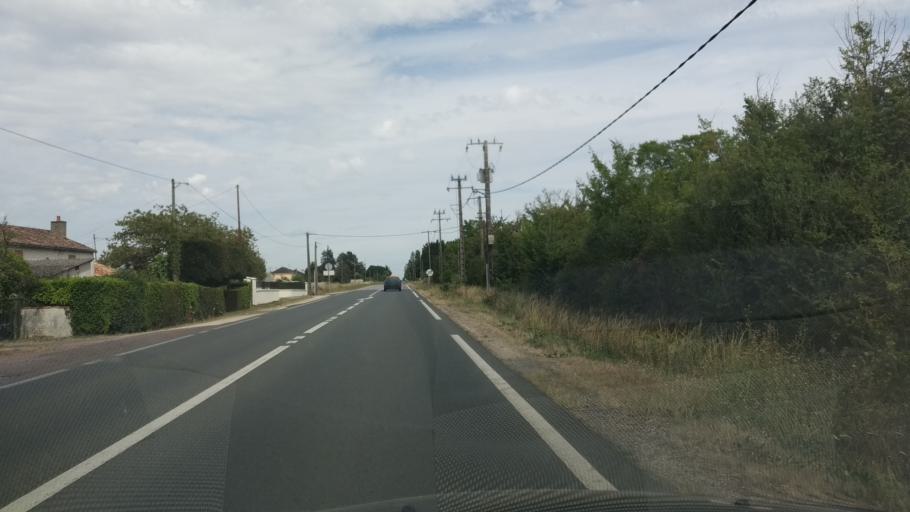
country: FR
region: Poitou-Charentes
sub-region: Departement de la Vienne
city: Mignaloux-Beauvoir
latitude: 46.5615
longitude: 0.4310
